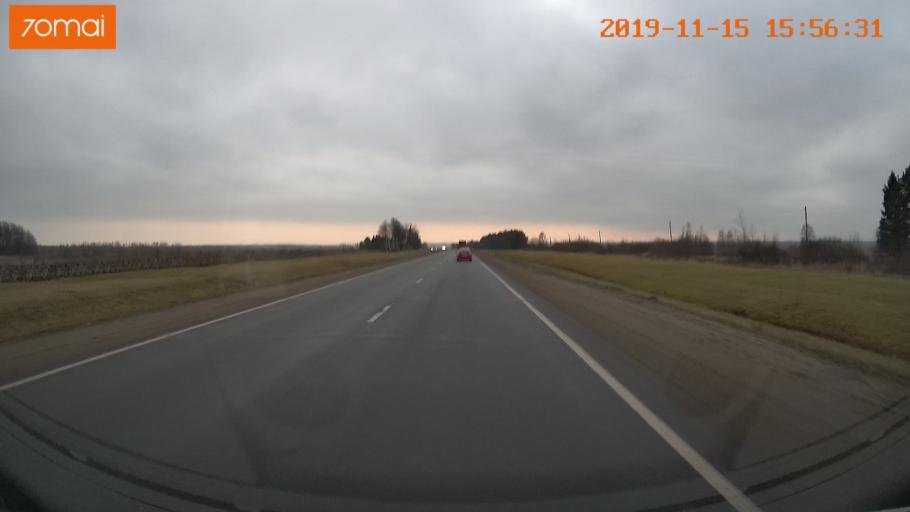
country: RU
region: Jaroslavl
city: Yaroslavl
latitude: 57.8413
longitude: 39.9728
